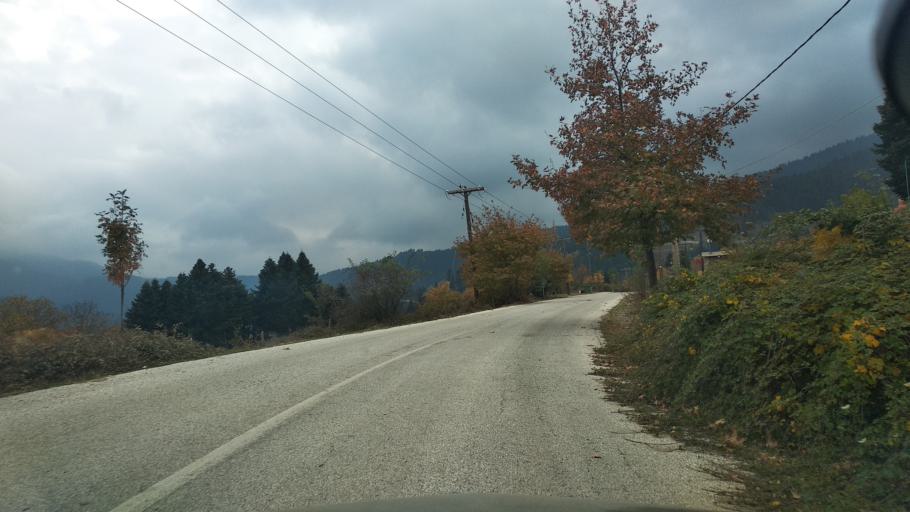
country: GR
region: Thessaly
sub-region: Trikala
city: Kalampaka
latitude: 39.5943
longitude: 21.4955
